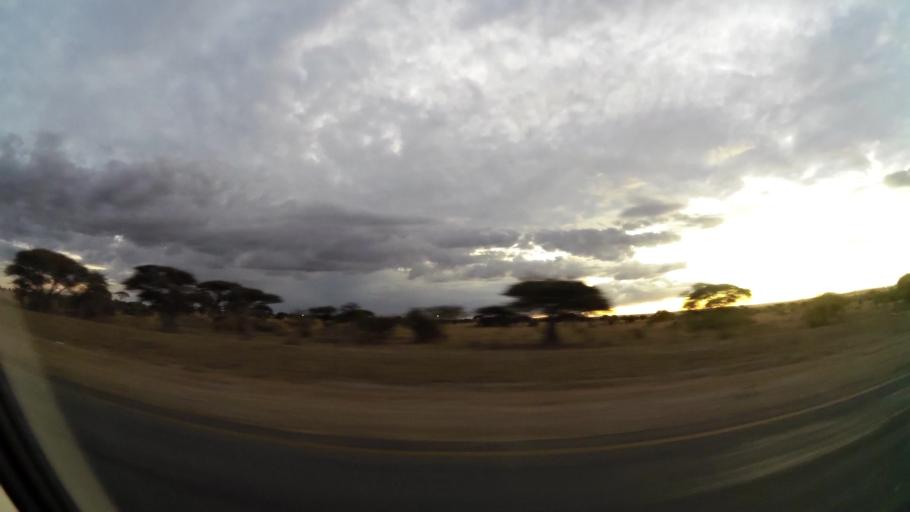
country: ZA
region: Limpopo
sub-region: Capricorn District Municipality
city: Polokwane
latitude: -23.8327
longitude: 29.4264
